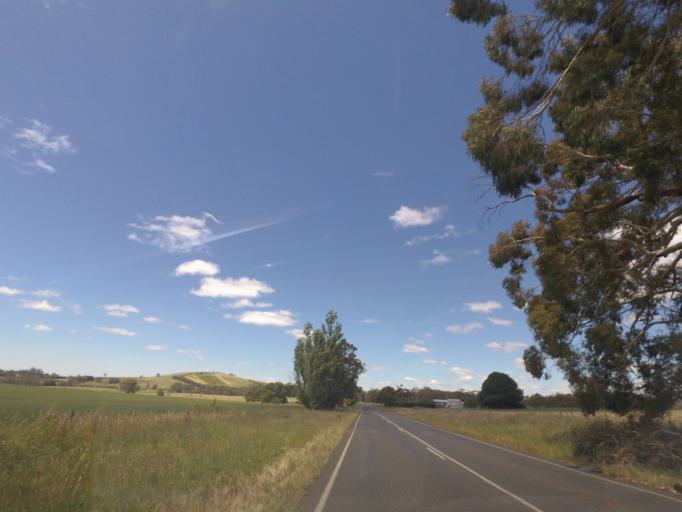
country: AU
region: Victoria
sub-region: Mount Alexander
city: Castlemaine
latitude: -37.3208
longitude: 144.2036
